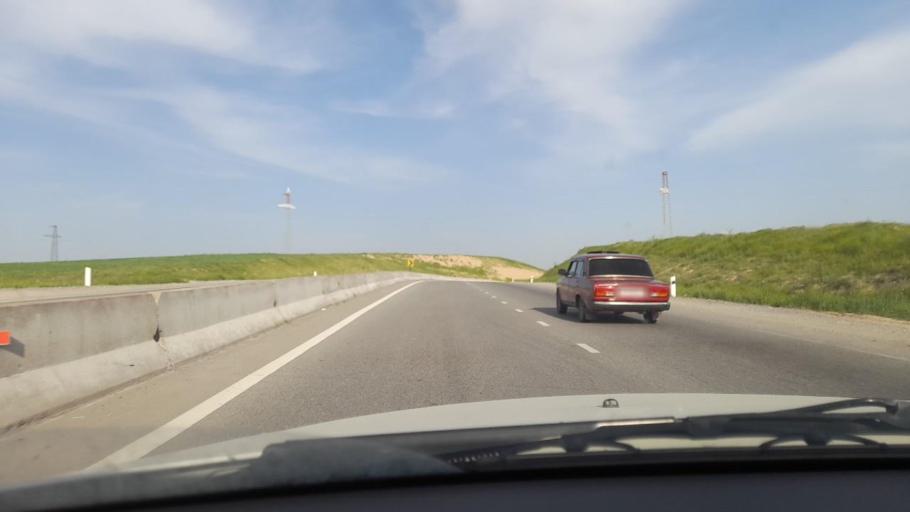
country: UZ
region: Jizzax
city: Jizzax
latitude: 40.0536
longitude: 67.7274
